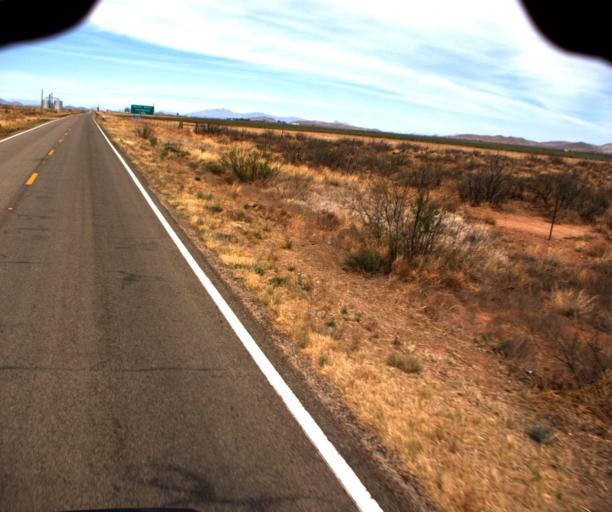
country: US
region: Arizona
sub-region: Cochise County
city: Bisbee
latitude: 31.7431
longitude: -109.6882
